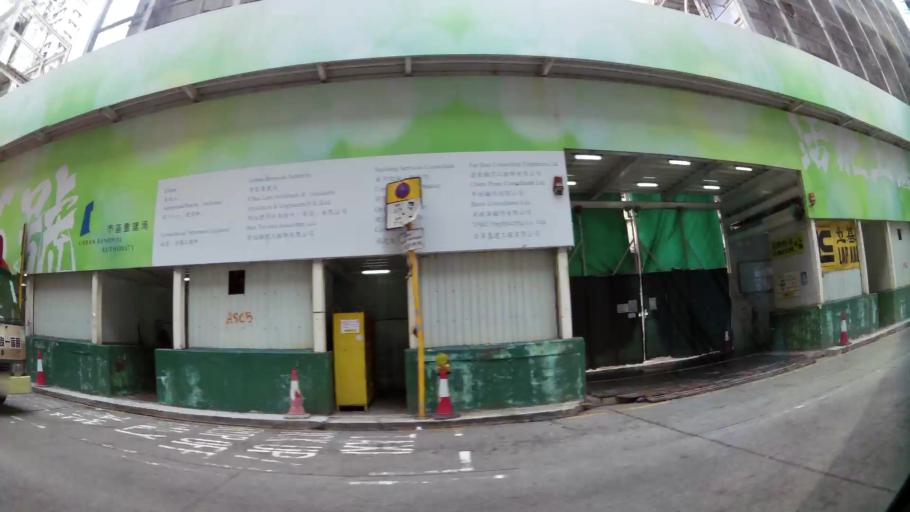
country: HK
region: Sham Shui Po
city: Sham Shui Po
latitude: 22.3195
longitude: 114.1681
